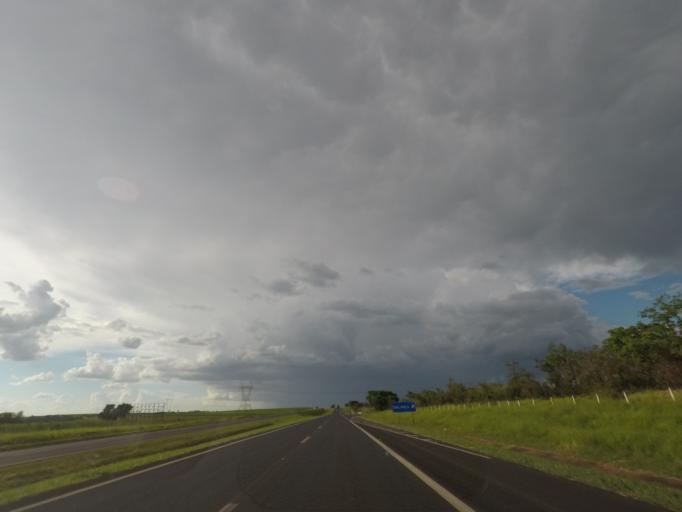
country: BR
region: Sao Paulo
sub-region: Jardinopolis
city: Jardinopolis
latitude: -21.0237
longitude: -47.8385
